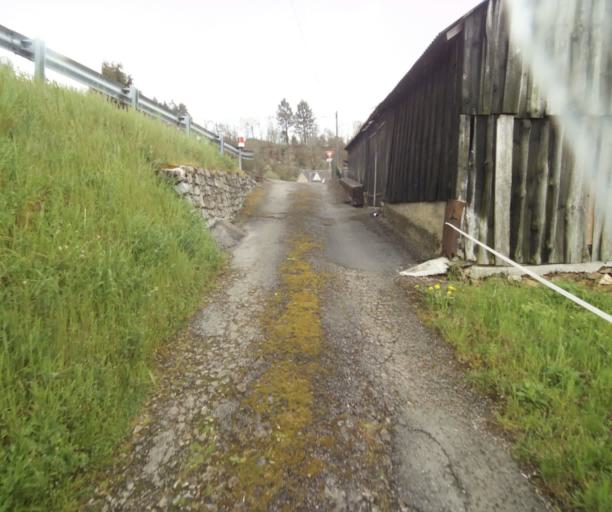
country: FR
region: Limousin
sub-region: Departement de la Correze
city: Tulle
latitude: 45.2879
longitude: 1.7987
